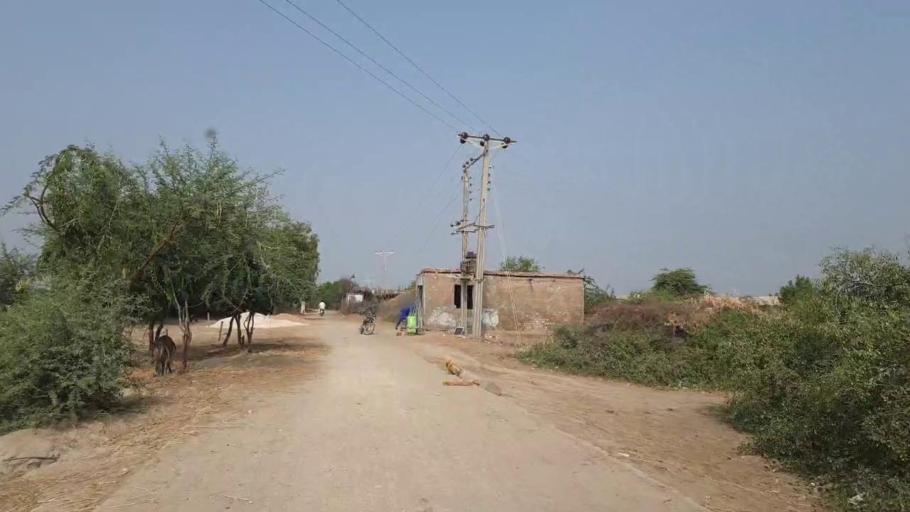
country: PK
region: Sindh
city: Kario
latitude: 24.9239
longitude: 68.6010
